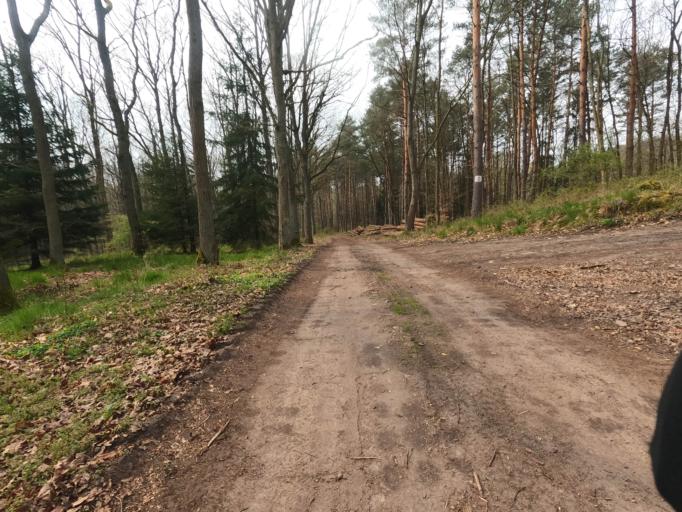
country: PL
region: West Pomeranian Voivodeship
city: Trzcinsko Zdroj
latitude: 52.9152
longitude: 14.5640
